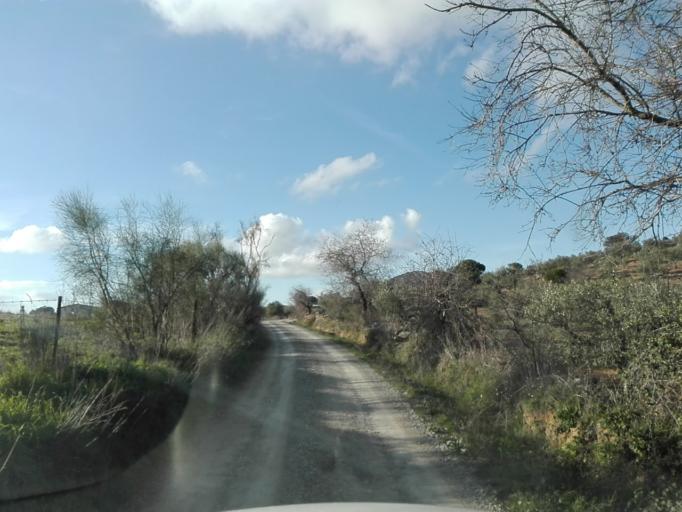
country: ES
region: Extremadura
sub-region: Provincia de Badajoz
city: Trasierra
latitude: 38.1834
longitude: -5.9835
